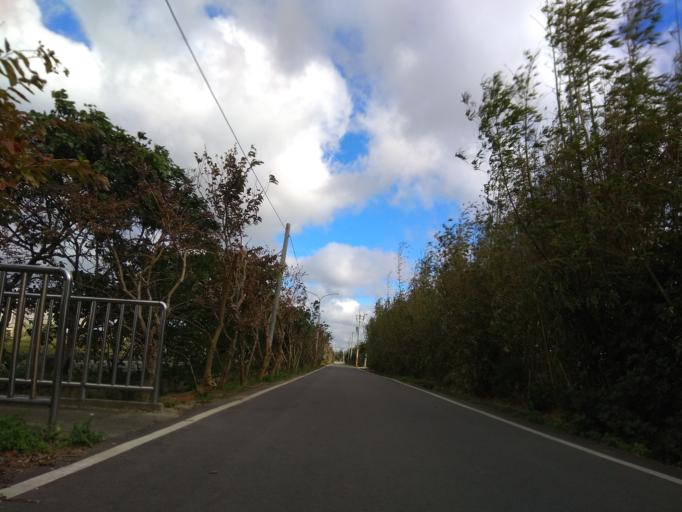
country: TW
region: Taiwan
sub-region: Hsinchu
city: Zhubei
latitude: 24.9740
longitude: 121.0886
